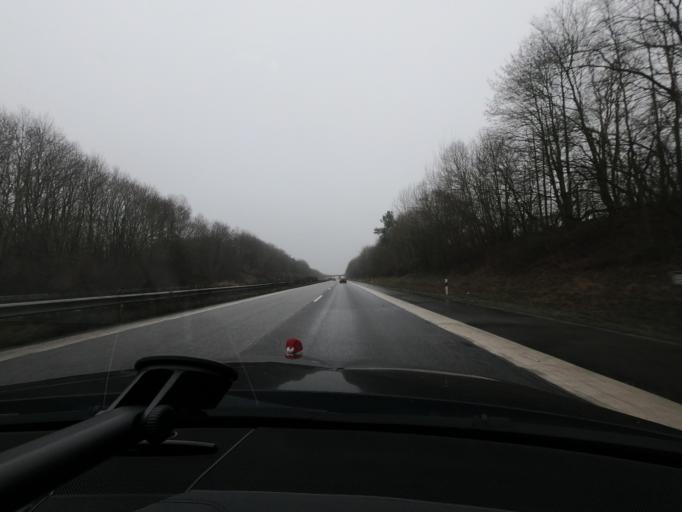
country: DE
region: Schleswig-Holstein
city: Selk
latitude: 54.4734
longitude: 9.5497
